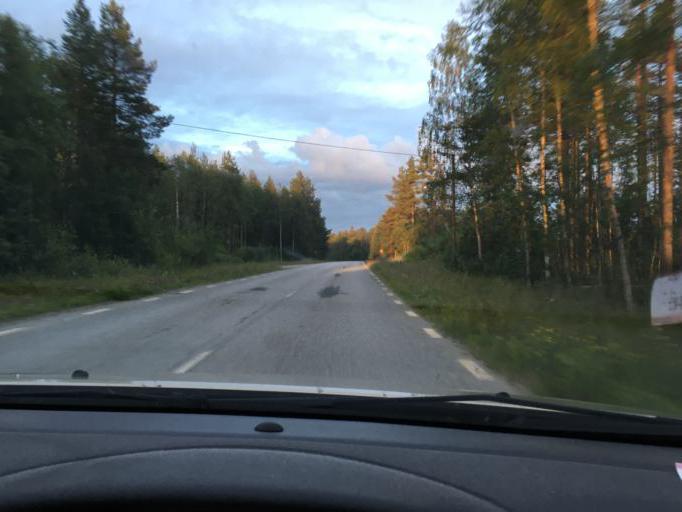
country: SE
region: Norrbotten
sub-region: Lulea Kommun
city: Ranea
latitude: 66.0447
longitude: 22.2883
